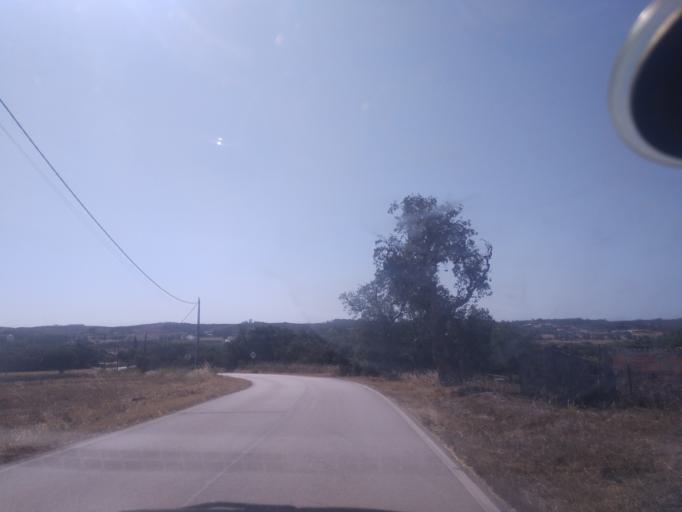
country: PT
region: Faro
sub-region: Aljezur
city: Aljezur
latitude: 37.2273
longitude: -8.8207
